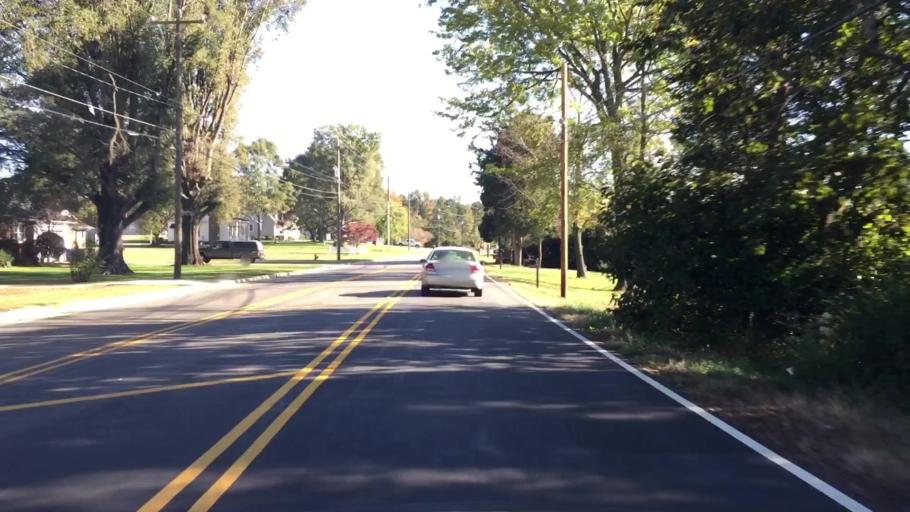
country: US
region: North Carolina
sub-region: Iredell County
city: Mooresville
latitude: 35.5968
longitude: -80.7816
